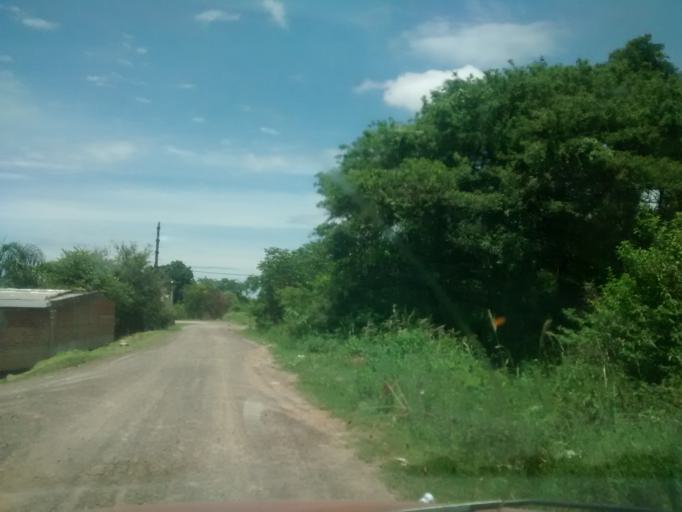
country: AR
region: Chaco
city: Resistencia
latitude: -27.4328
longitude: -58.9771
